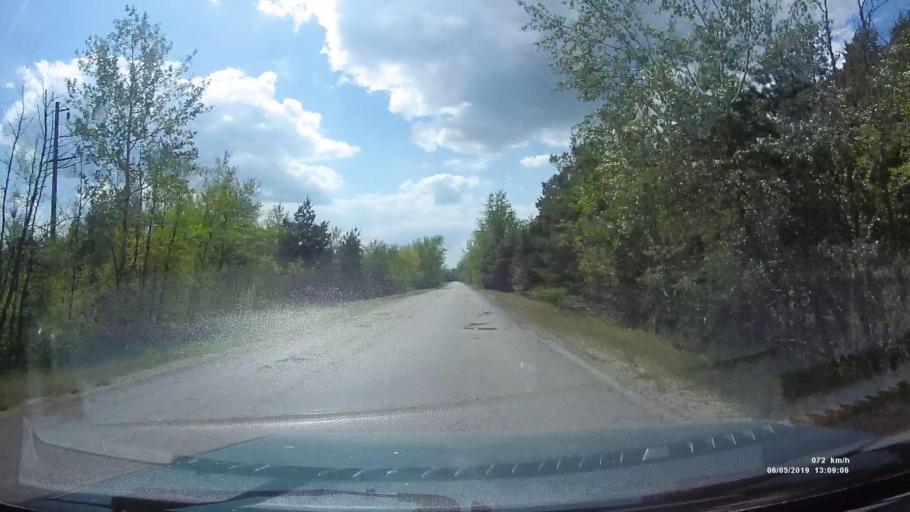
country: RU
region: Rostov
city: Ust'-Donetskiy
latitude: 47.7710
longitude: 40.9882
